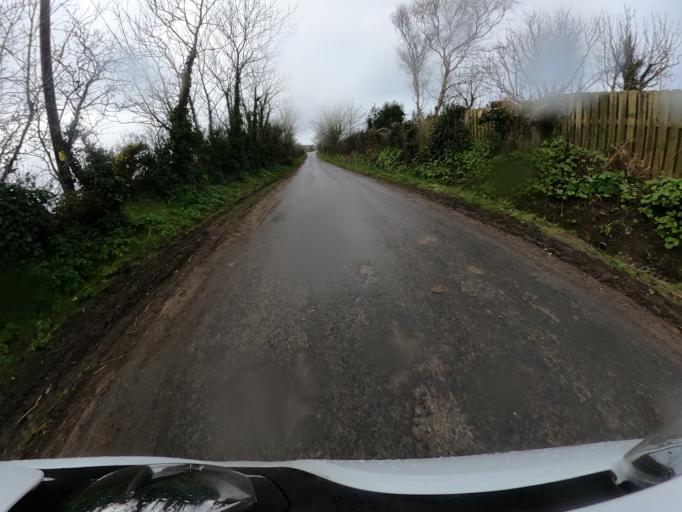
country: IM
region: Ramsey
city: Ramsey
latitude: 54.3834
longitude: -4.4670
